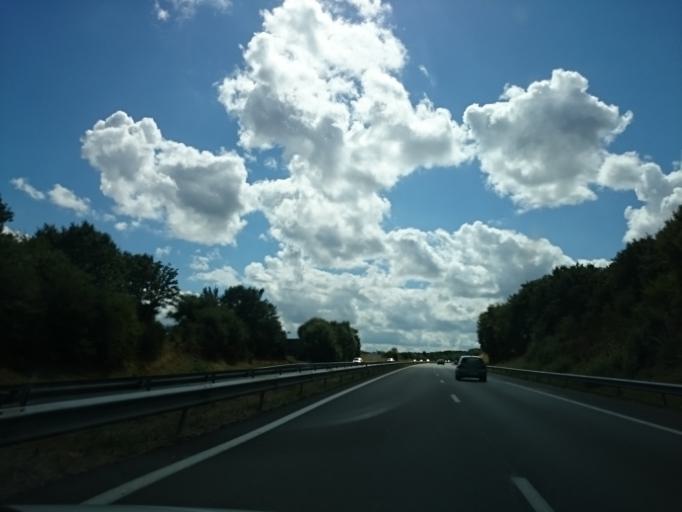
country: FR
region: Pays de la Loire
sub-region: Departement de Maine-et-Loire
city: Durtal
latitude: 47.6782
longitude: -0.2548
